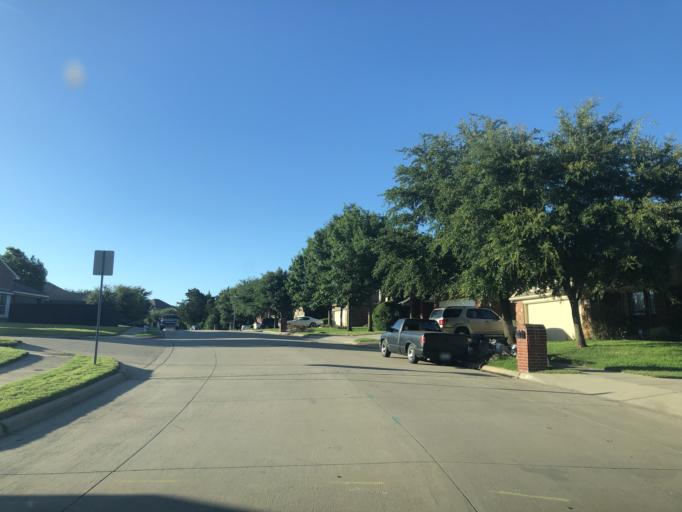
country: US
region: Texas
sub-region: Dallas County
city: Duncanville
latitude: 32.6545
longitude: -96.9503
